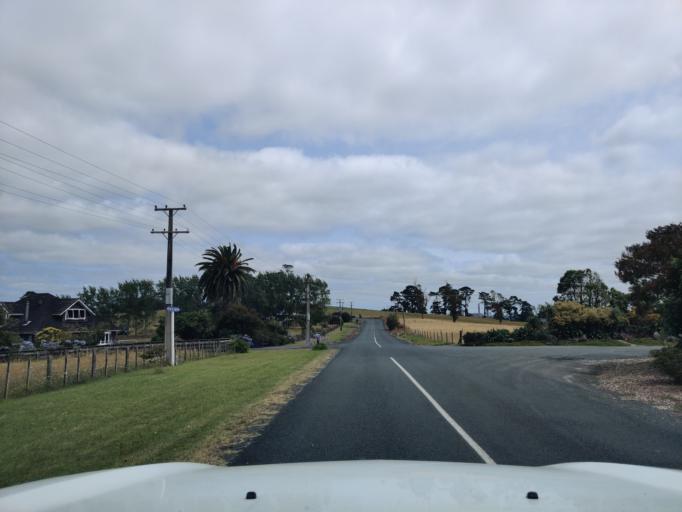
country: NZ
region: Waikato
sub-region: Waikato District
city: Te Kauwhata
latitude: -37.5121
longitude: 175.1768
